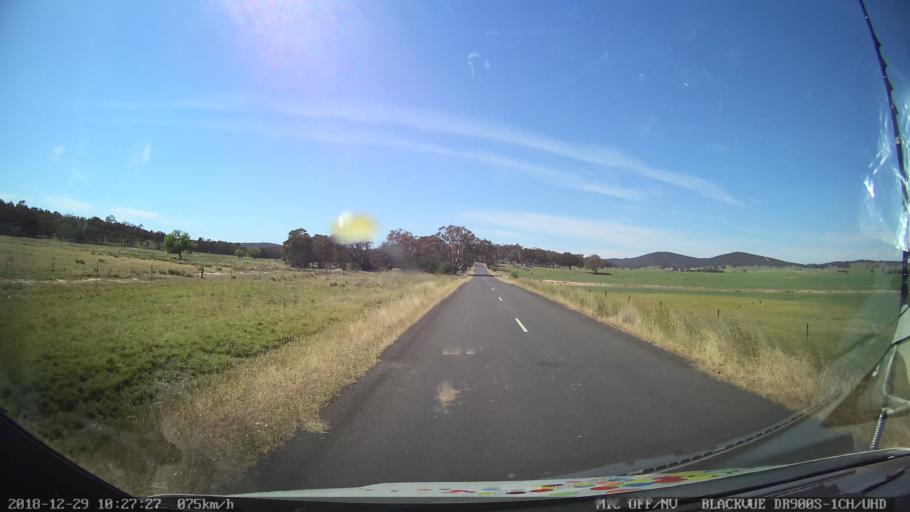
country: AU
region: New South Wales
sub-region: Yass Valley
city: Gundaroo
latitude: -34.9342
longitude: 149.4503
